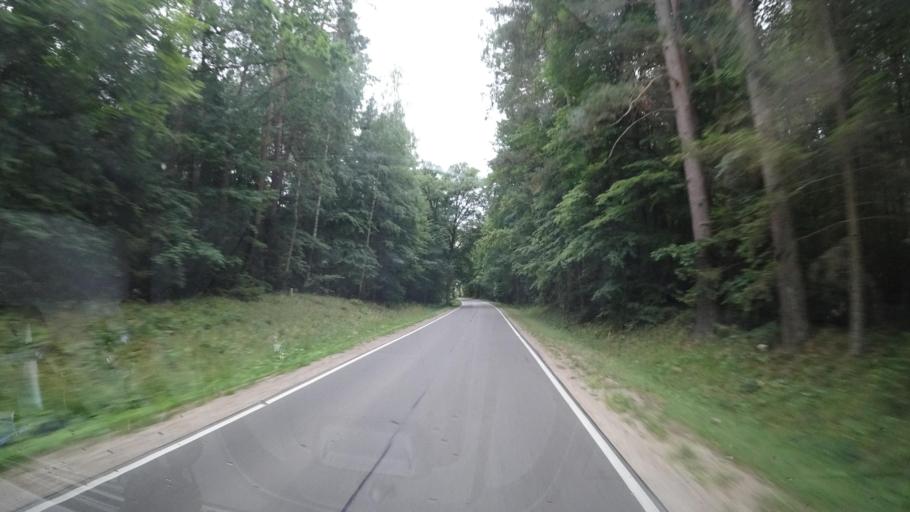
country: PL
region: Warmian-Masurian Voivodeship
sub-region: Powiat gizycki
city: Ryn
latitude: 53.8834
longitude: 21.5787
